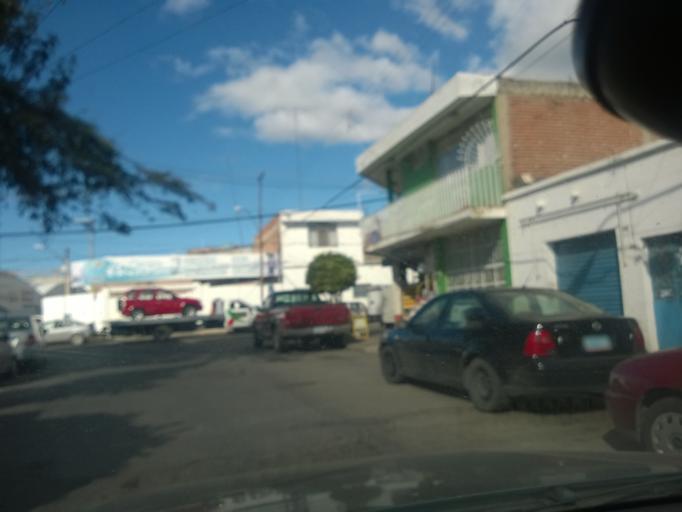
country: MX
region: Guanajuato
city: Leon
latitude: 21.1360
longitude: -101.6866
